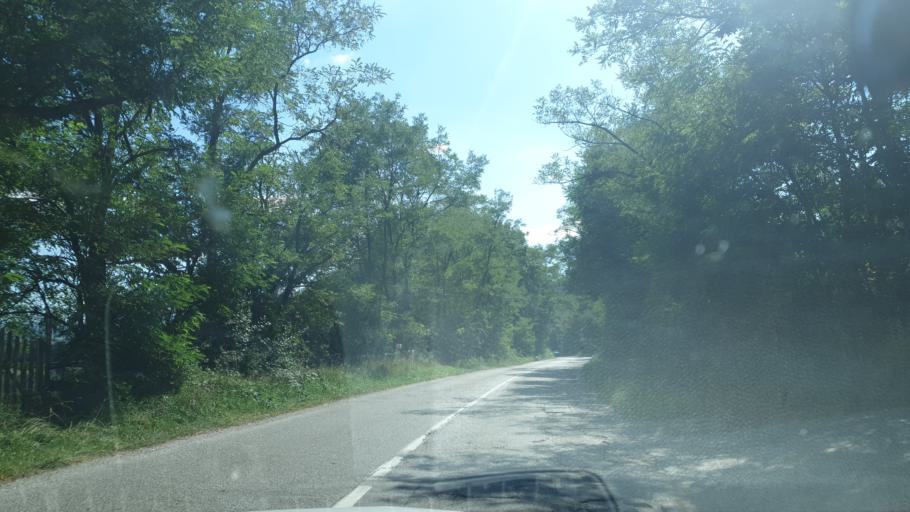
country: RS
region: Central Serbia
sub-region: Zlatiborski Okrug
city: Kosjeric
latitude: 44.0646
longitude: 20.0218
